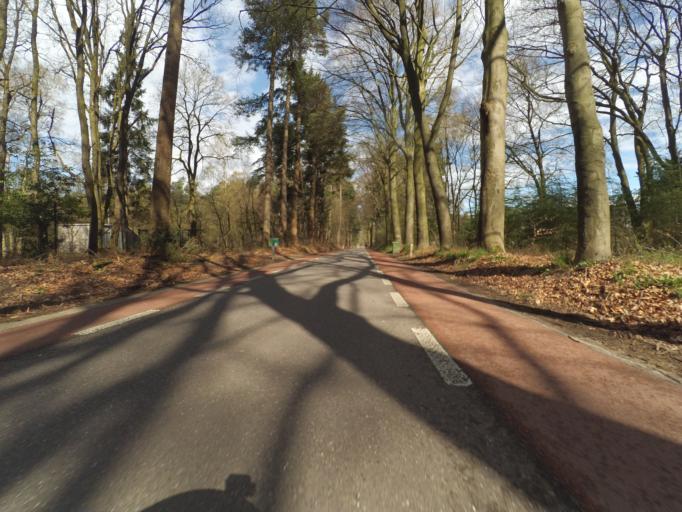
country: NL
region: Gelderland
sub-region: Gemeente Apeldoorn
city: Beekbergen
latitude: 52.1067
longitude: 5.8777
